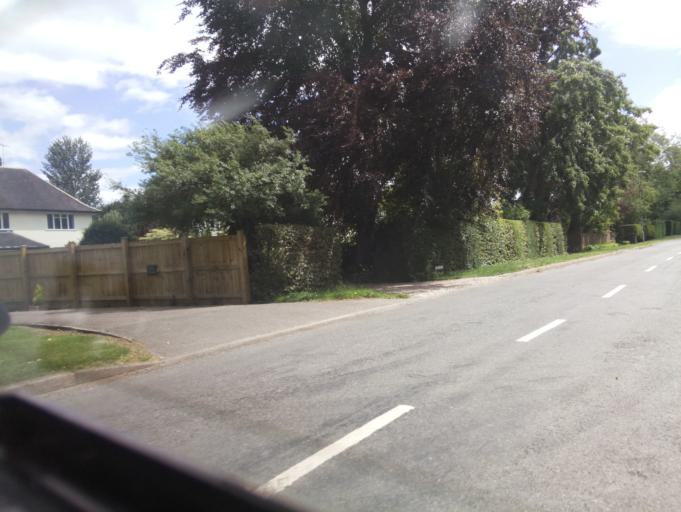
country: GB
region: England
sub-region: Nottinghamshire
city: Cotgrave
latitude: 52.8730
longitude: -1.0733
